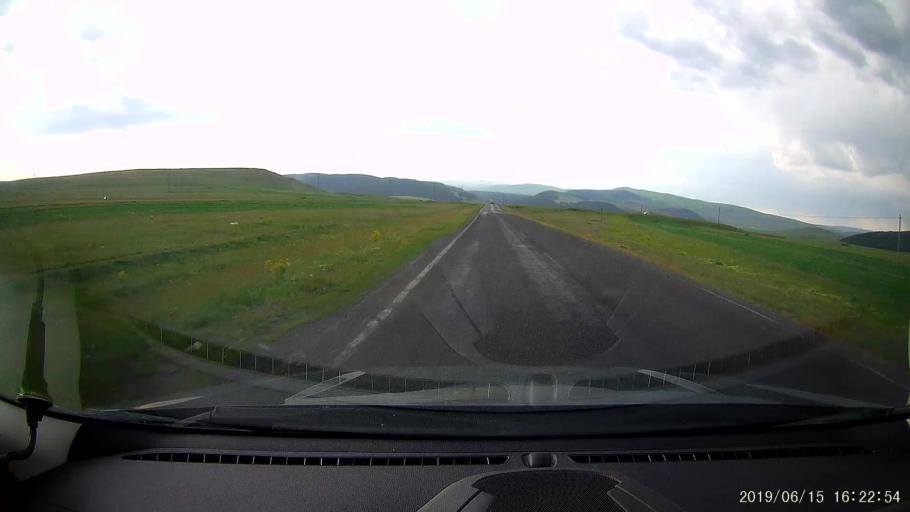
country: TR
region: Ardahan
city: Hanak
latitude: 41.1836
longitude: 42.8558
